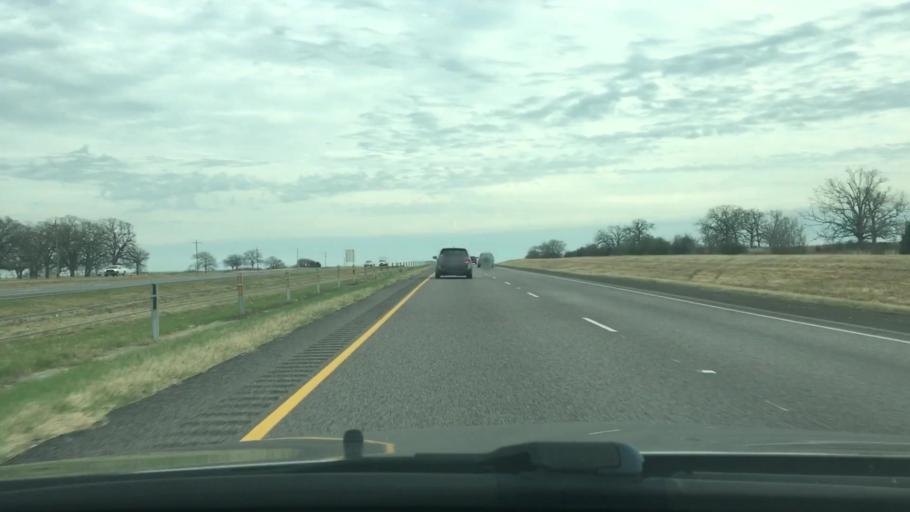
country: US
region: Texas
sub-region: Madison County
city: Madisonville
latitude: 30.9525
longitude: -95.8652
